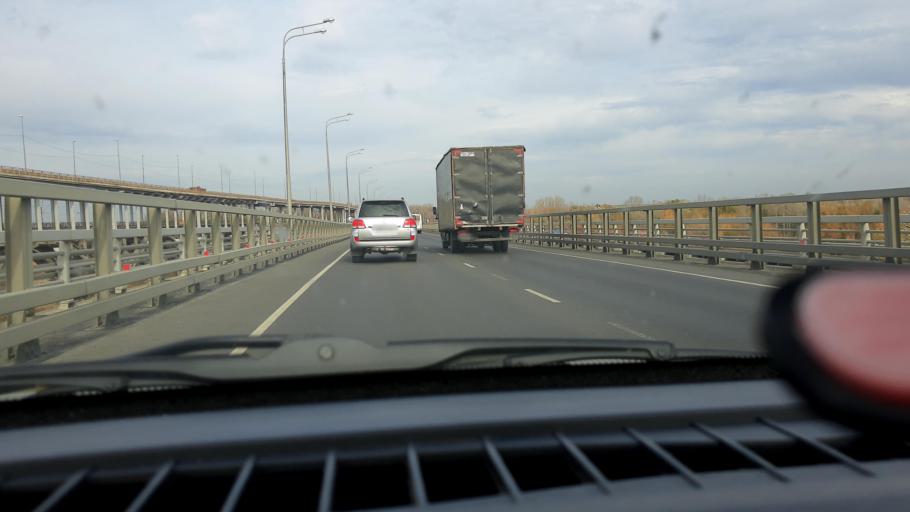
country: RU
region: Nizjnij Novgorod
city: Neklyudovo
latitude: 56.3571
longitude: 43.9287
